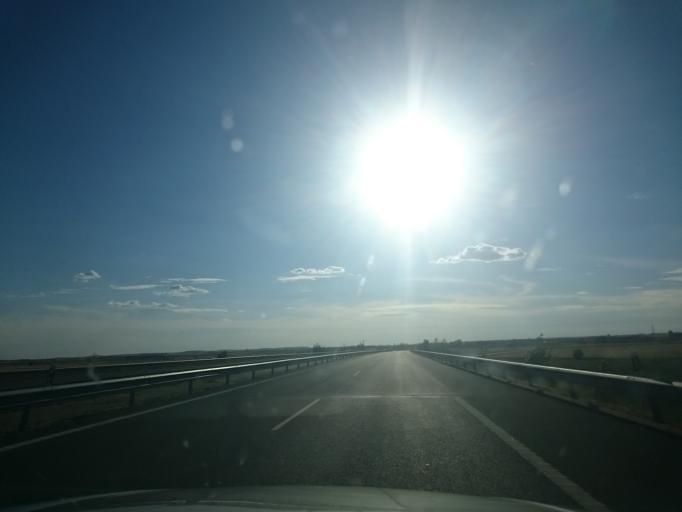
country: ES
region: Castille and Leon
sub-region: Provincia de Burgos
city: Padilla de Abajo
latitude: 42.4008
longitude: -4.1623
